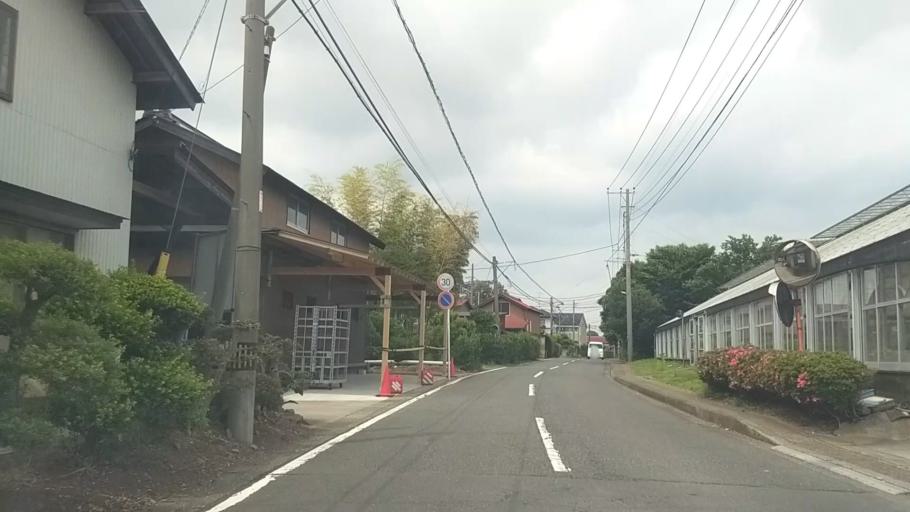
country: JP
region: Kanagawa
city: Chigasaki
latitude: 35.3906
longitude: 139.4143
